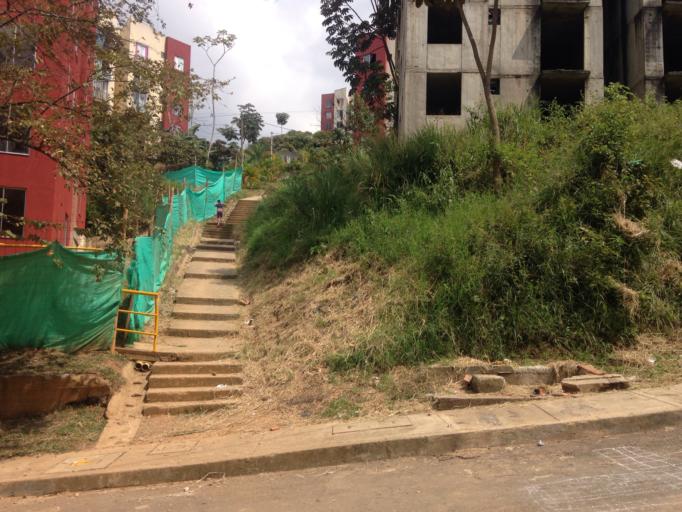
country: CO
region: Valle del Cauca
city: Cali
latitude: 3.3694
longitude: -76.5547
